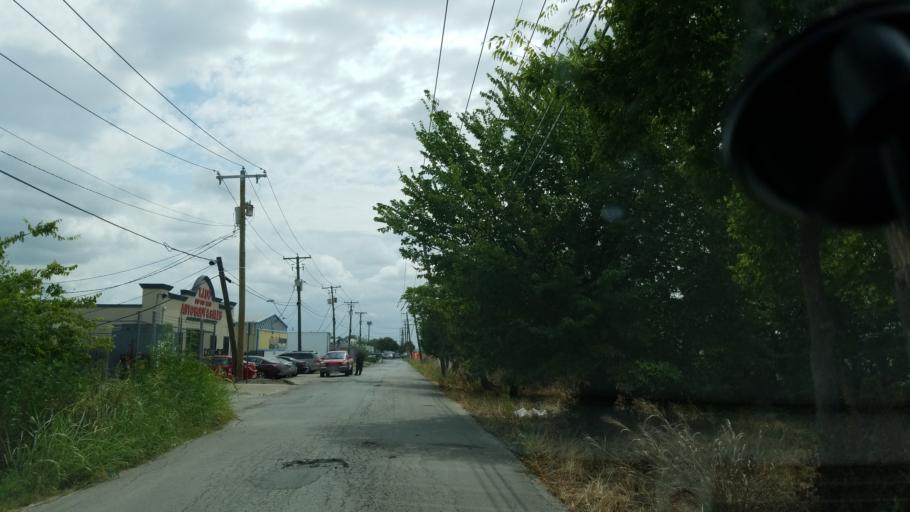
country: US
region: Texas
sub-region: Dallas County
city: Grand Prairie
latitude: 32.7456
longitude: -96.9897
